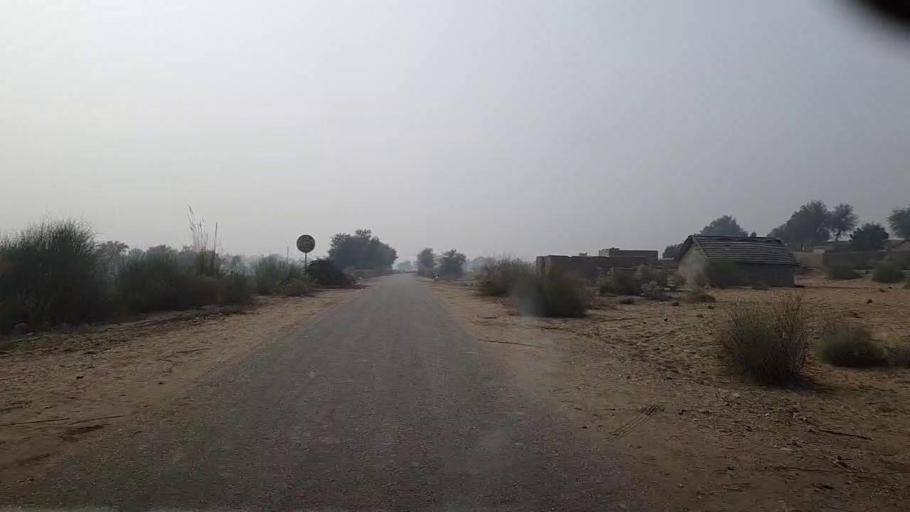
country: PK
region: Sindh
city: Kandiari
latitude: 26.9807
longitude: 68.6013
